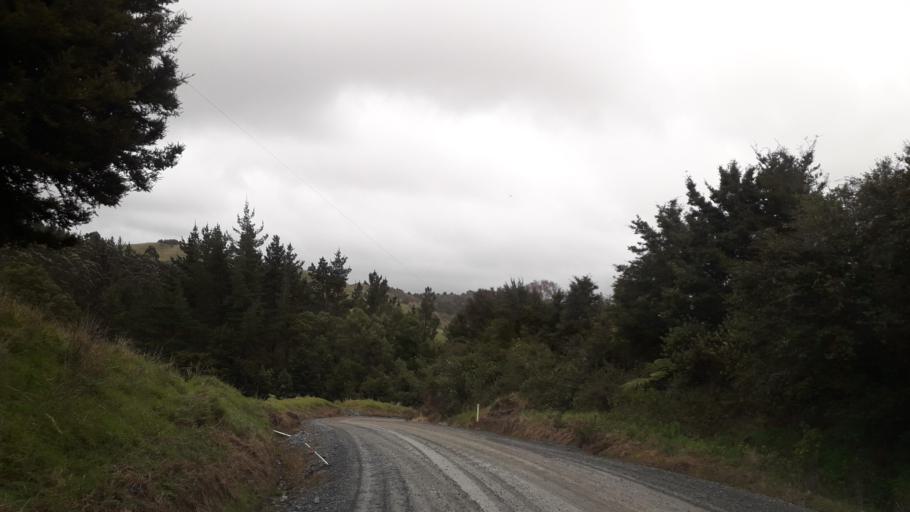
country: NZ
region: Northland
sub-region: Far North District
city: Kerikeri
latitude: -35.1278
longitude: 173.7437
